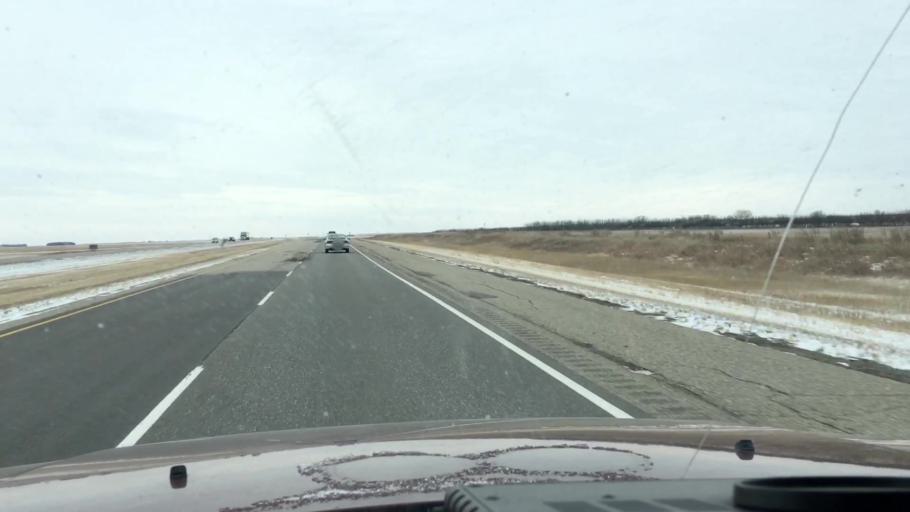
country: CA
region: Saskatchewan
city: Saskatoon
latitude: 51.4679
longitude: -106.2437
